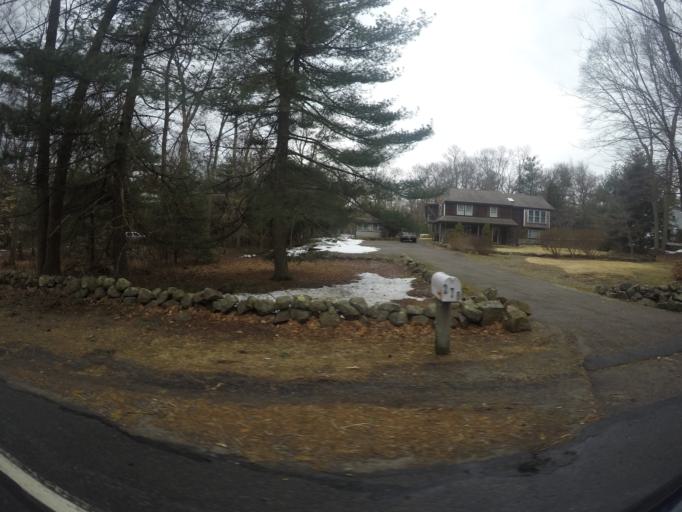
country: US
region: Massachusetts
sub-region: Bristol County
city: Easton
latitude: 42.0596
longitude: -71.1667
